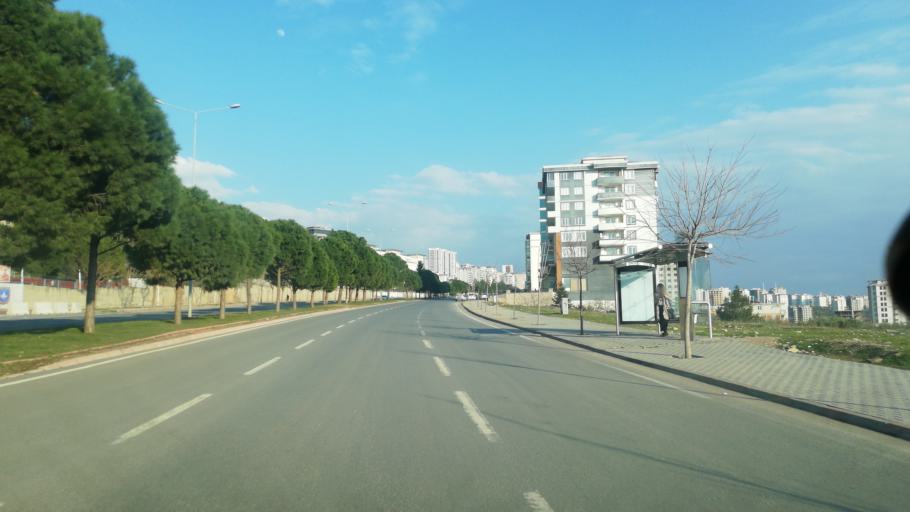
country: TR
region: Kahramanmaras
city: Kahramanmaras
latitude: 37.5999
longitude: 36.8328
